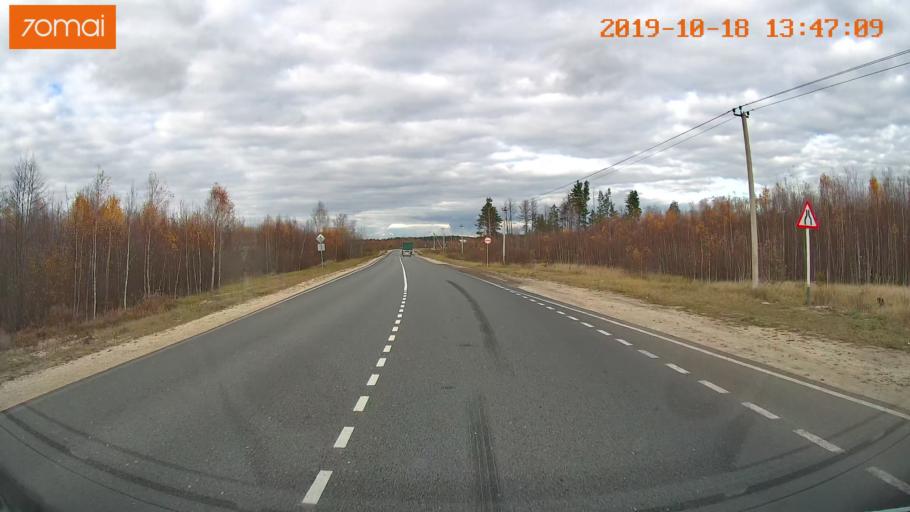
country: RU
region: Rjazan
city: Solotcha
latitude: 54.9706
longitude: 39.9515
